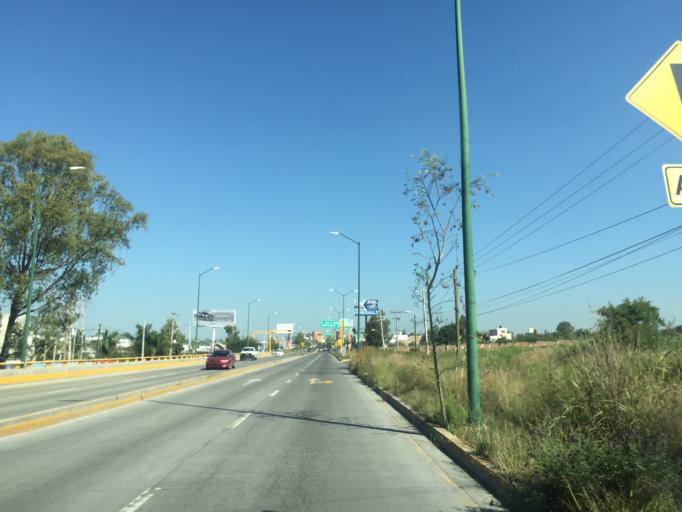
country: MX
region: Guanajuato
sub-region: Leon
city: La Ermita
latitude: 21.1598
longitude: -101.7235
